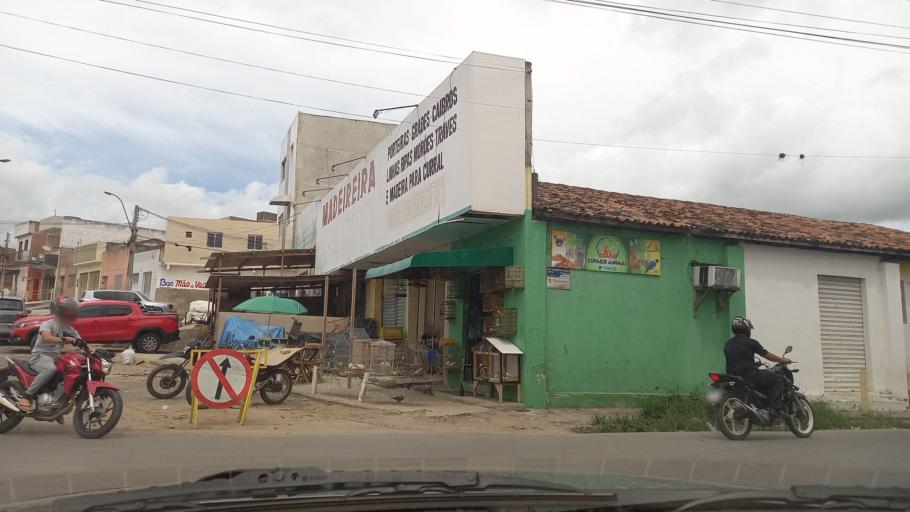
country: BR
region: Pernambuco
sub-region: Gravata
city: Gravata
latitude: -8.2008
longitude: -35.5692
